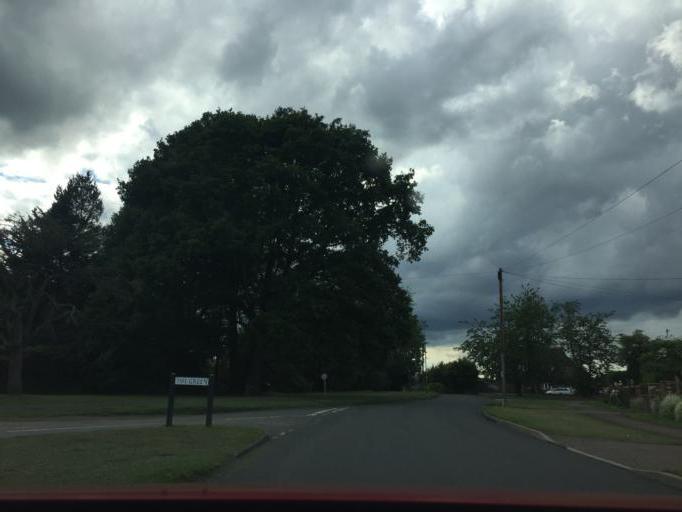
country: GB
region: England
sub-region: Hertfordshire
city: Harpenden
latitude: 51.8586
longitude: -0.3432
